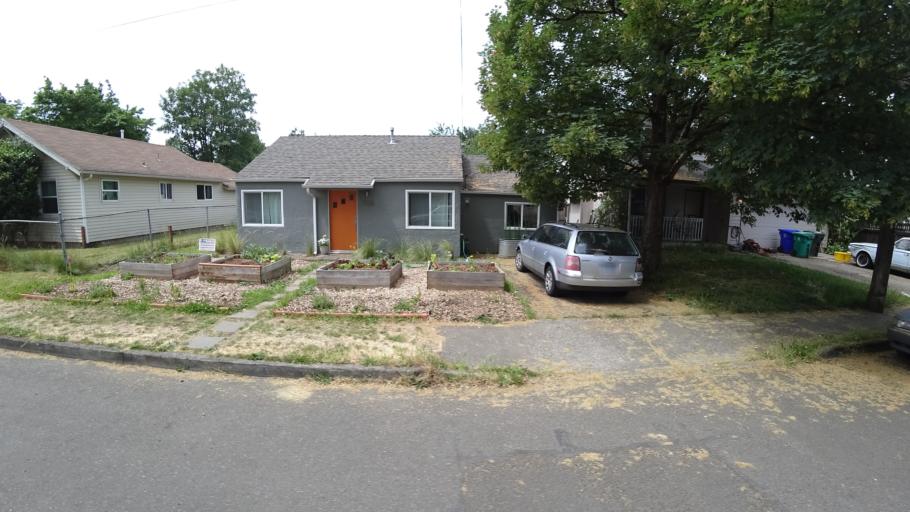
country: US
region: Oregon
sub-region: Multnomah County
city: Lents
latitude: 45.4696
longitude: -122.6023
